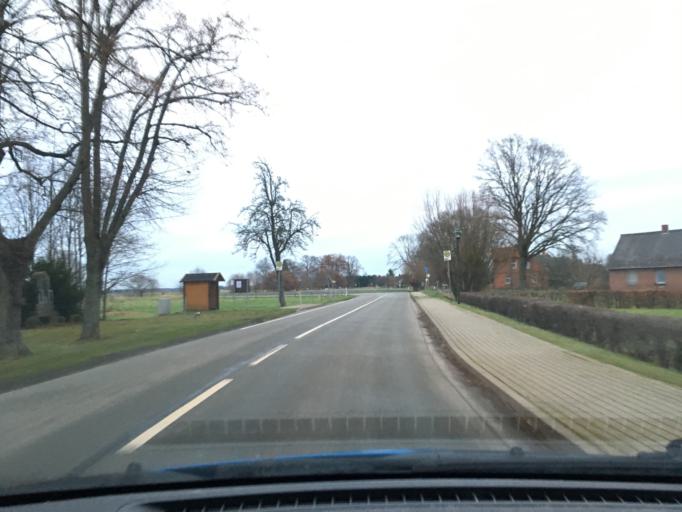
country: DE
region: Lower Saxony
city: Neu Darchau
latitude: 53.2399
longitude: 10.8961
